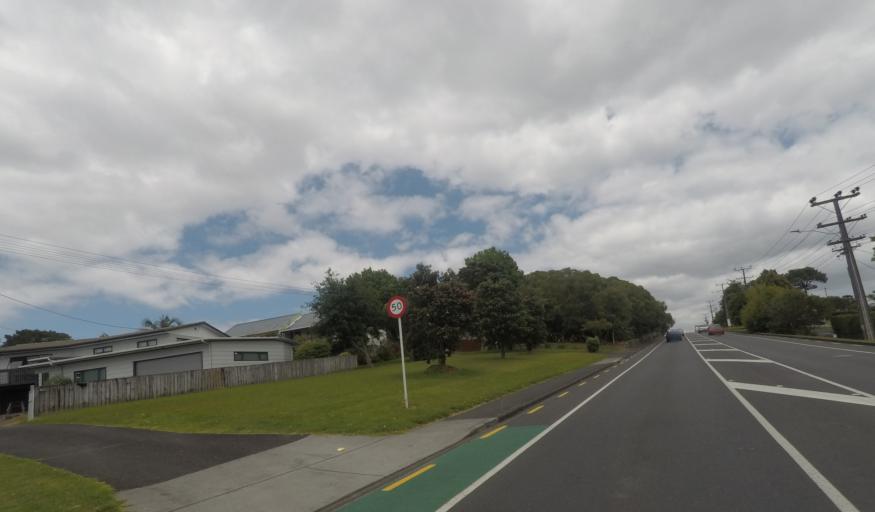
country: NZ
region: Auckland
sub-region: Auckland
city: Rosebank
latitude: -36.8291
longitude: 174.6074
